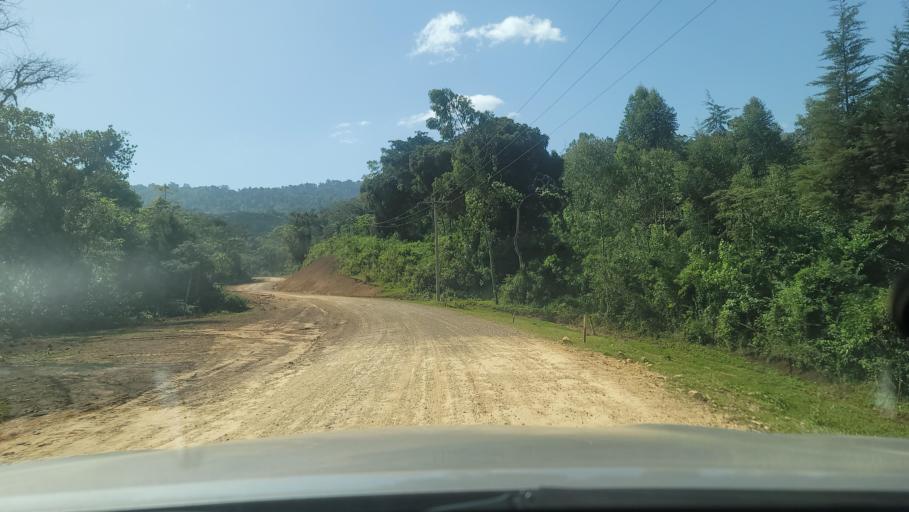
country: ET
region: Oromiya
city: Agaro
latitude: 7.7931
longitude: 36.3885
